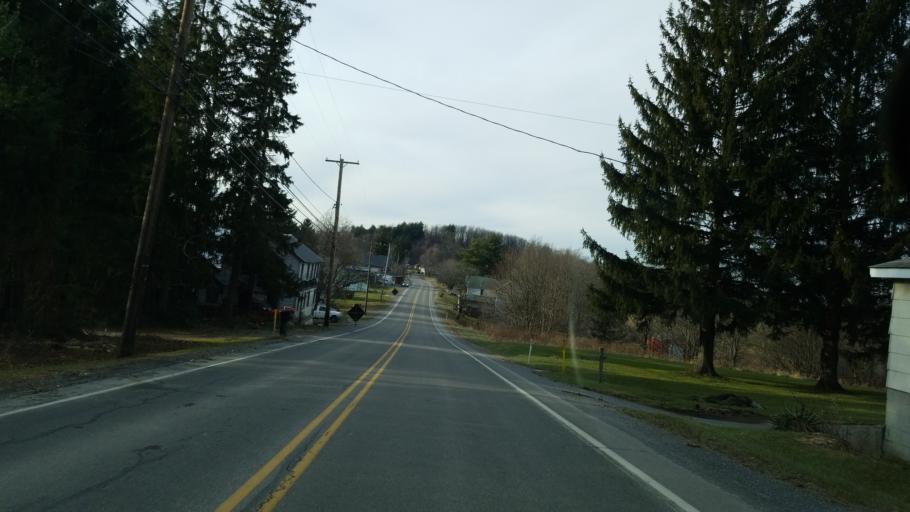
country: US
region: Pennsylvania
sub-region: Clearfield County
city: Sandy
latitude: 41.0503
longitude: -78.7058
